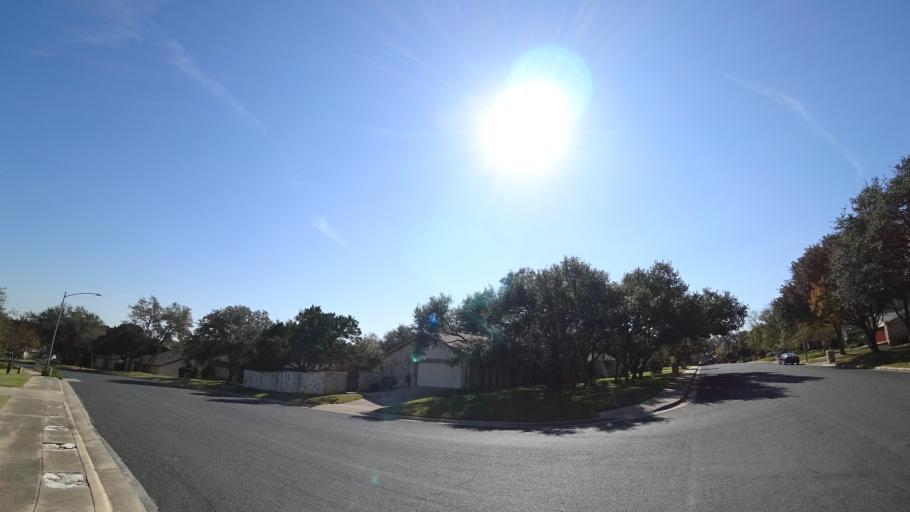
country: US
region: Texas
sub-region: Williamson County
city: Jollyville
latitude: 30.3736
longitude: -97.7737
